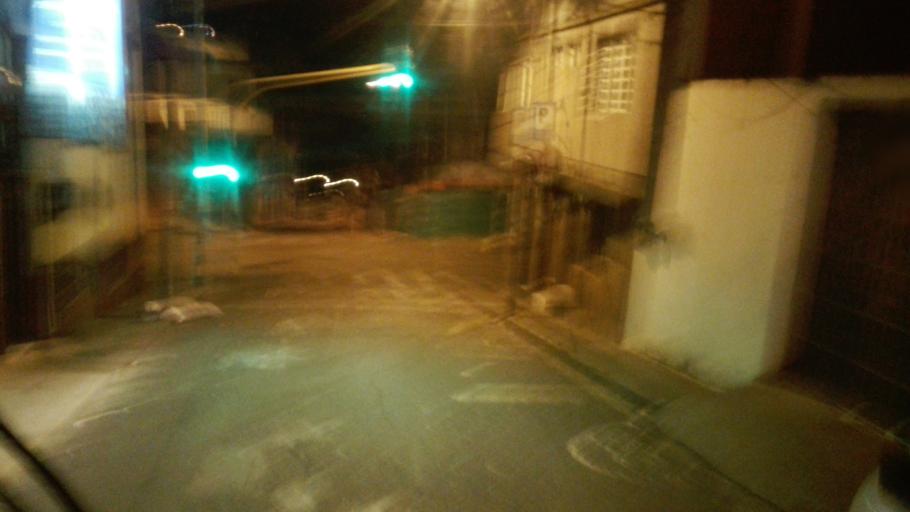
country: CO
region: Risaralda
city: Pereira
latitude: 4.8169
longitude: -75.6922
